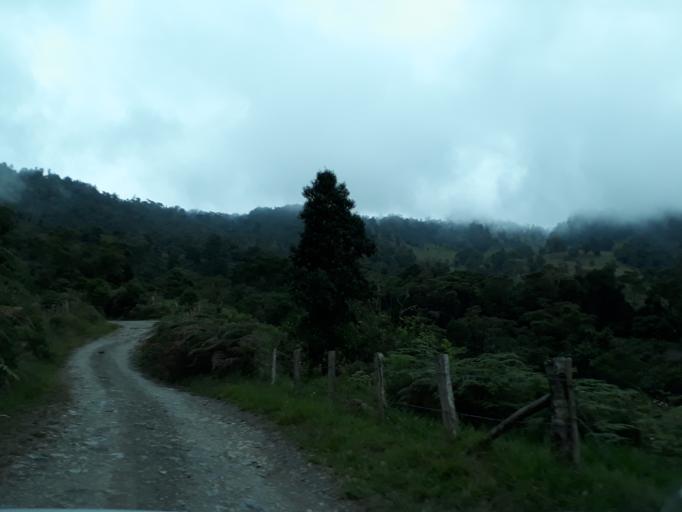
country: CO
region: Boyaca
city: Muzo
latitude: 5.3808
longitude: -74.0792
